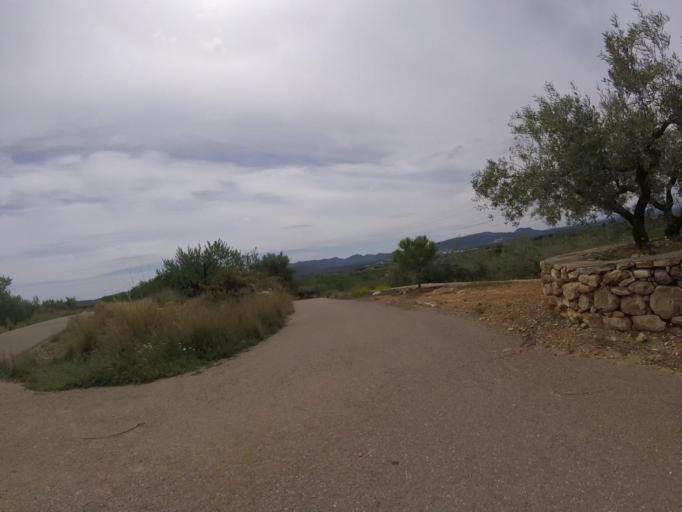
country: ES
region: Valencia
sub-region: Provincia de Castello
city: Benlloch
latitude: 40.1959
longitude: -0.0069
